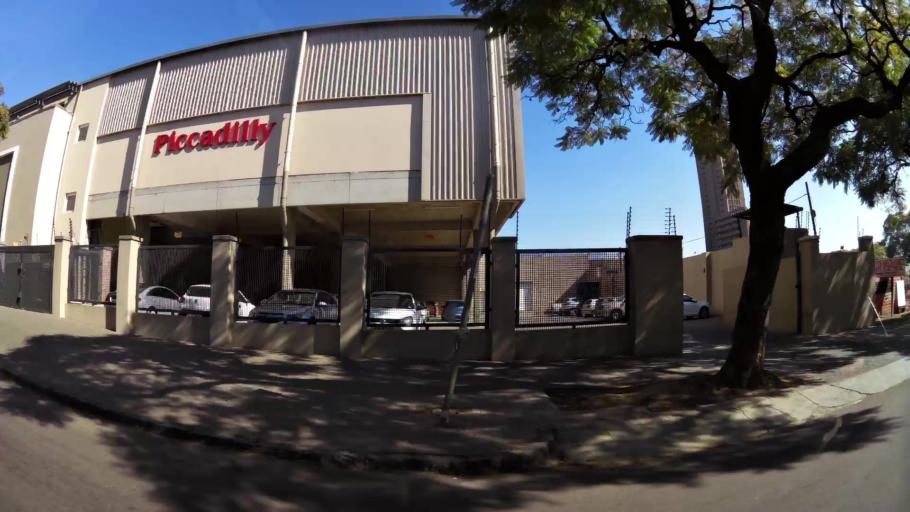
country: ZA
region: Gauteng
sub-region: City of Tshwane Metropolitan Municipality
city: Pretoria
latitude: -25.7463
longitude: 28.1806
